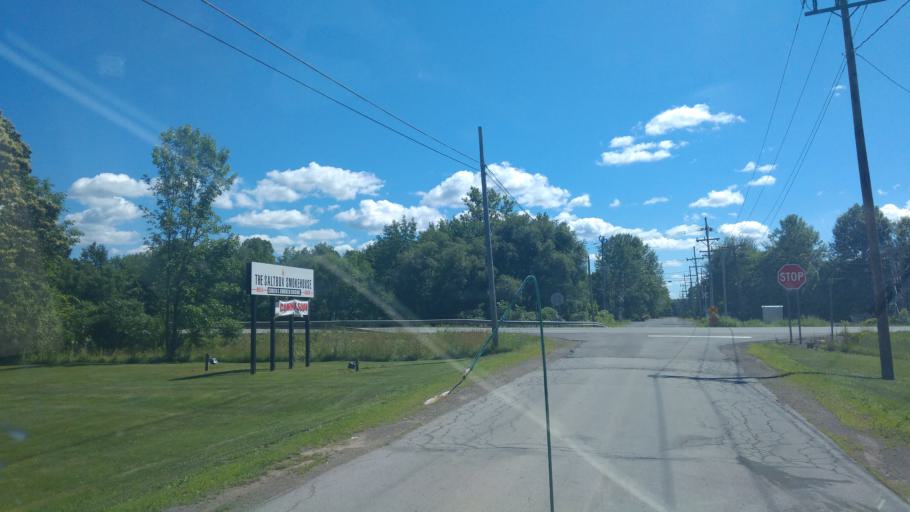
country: US
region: New York
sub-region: Wayne County
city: Sodus
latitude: 43.2236
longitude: -77.0228
